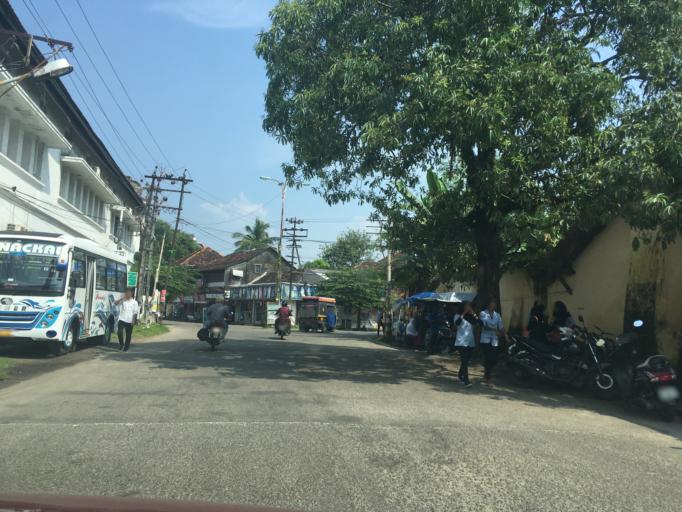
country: IN
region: Kerala
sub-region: Ernakulam
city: Cochin
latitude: 9.9680
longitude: 76.2465
